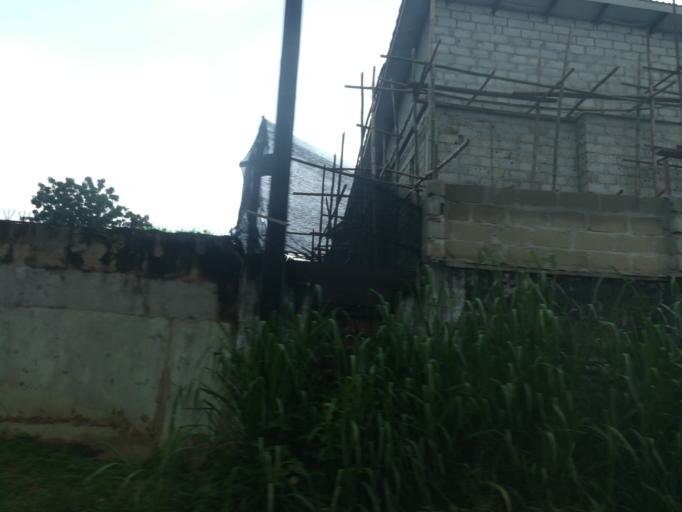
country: NG
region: Lagos
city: Ojota
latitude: 6.5681
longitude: 3.3689
